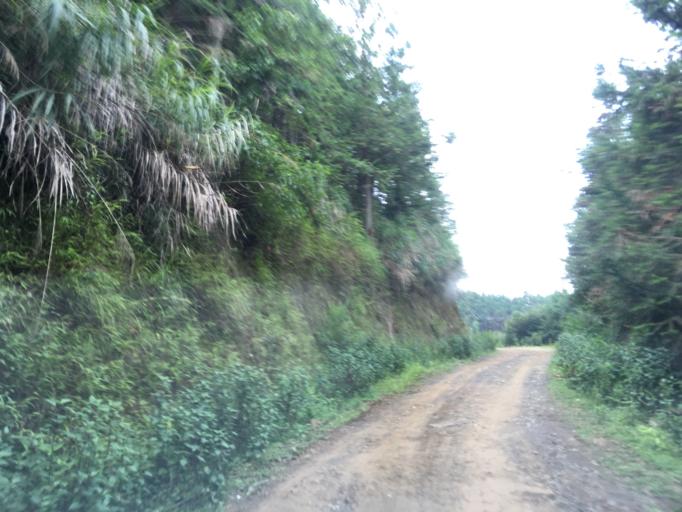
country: CN
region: Guangxi Zhuangzu Zizhiqu
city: Xinzhou
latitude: 24.8776
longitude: 105.8457
